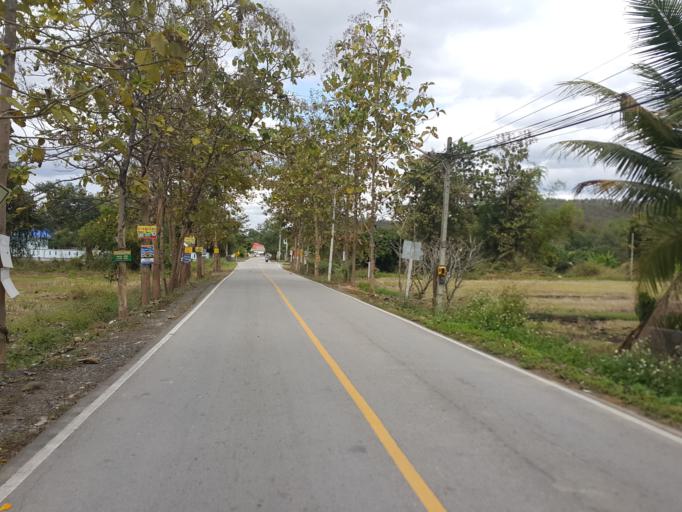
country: TH
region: Chiang Mai
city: San Sai
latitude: 18.8576
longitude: 99.1417
